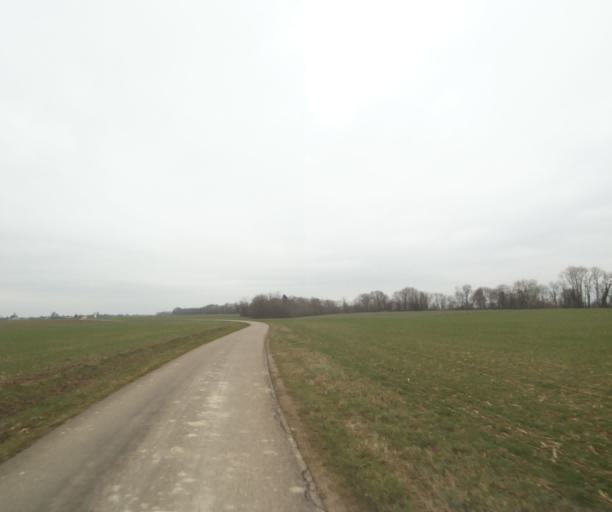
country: FR
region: Champagne-Ardenne
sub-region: Departement de la Haute-Marne
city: Villiers-en-Lieu
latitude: 48.6379
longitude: 4.7903
